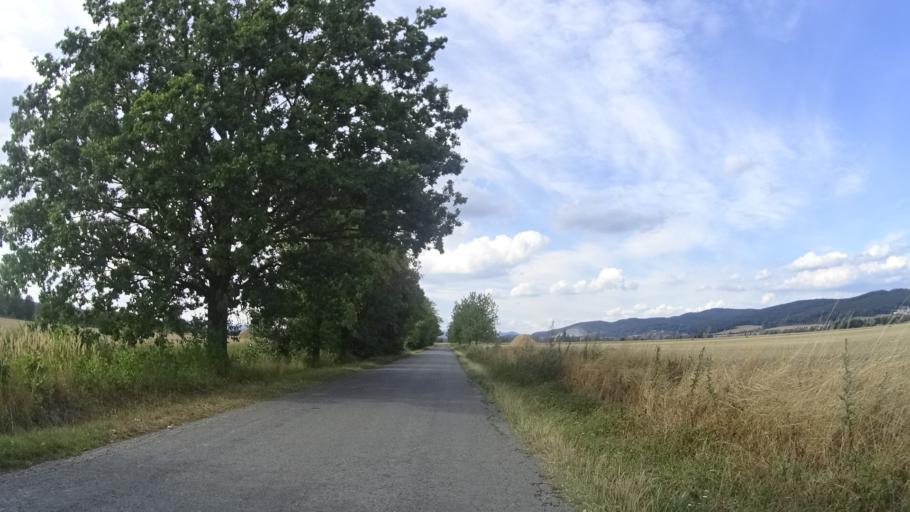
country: CZ
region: Olomoucky
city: Dubicko
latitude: 49.8136
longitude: 16.9428
